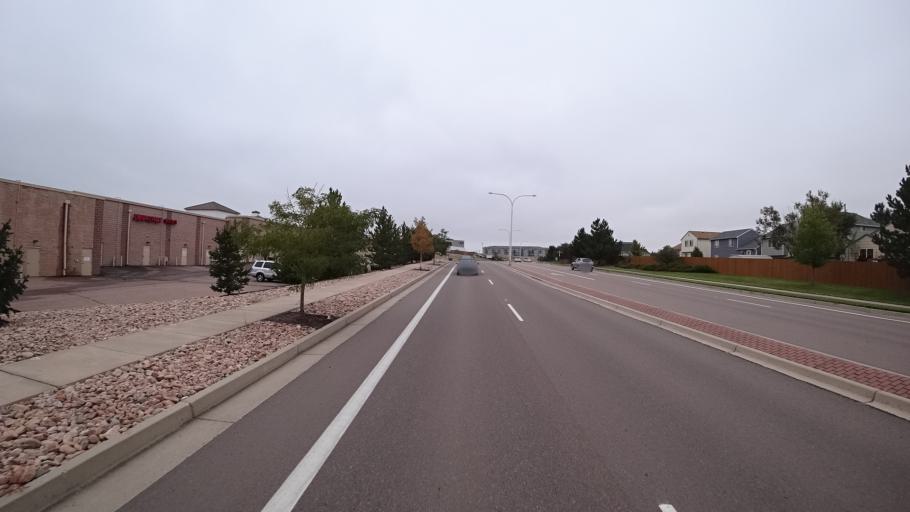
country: US
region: Colorado
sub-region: El Paso County
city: Cimarron Hills
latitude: 38.9144
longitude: -104.7166
